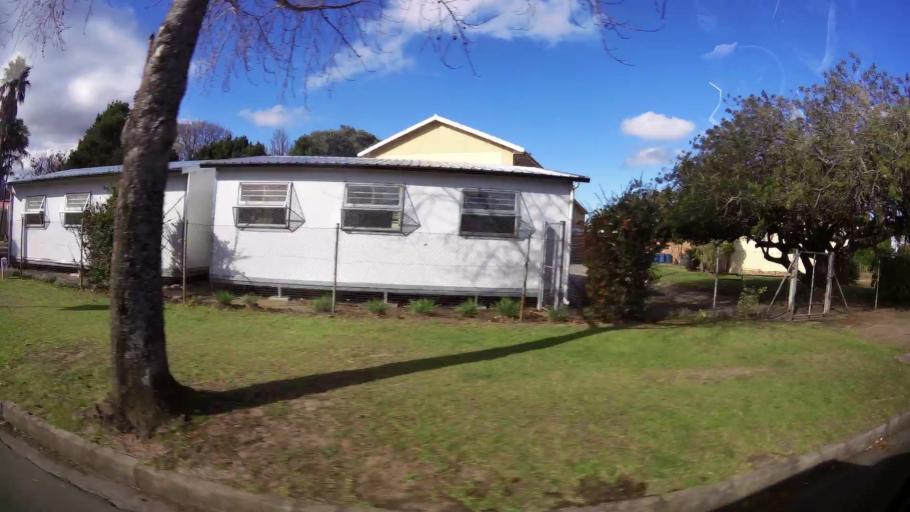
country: ZA
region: Western Cape
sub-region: Eden District Municipality
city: George
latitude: -33.9571
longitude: 22.4750
